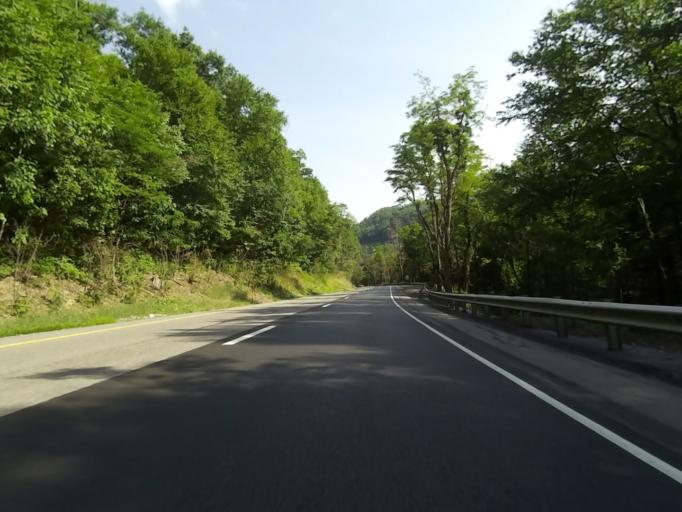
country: US
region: Pennsylvania
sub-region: Centre County
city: Stormstown
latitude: 40.8326
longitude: -78.1140
